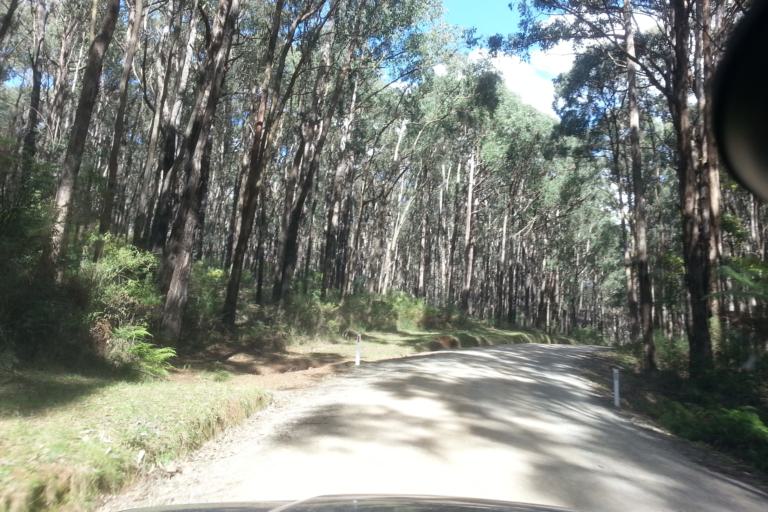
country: AU
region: Victoria
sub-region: Yarra Ranges
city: Mount Dandenong
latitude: -37.8304
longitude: 145.3985
